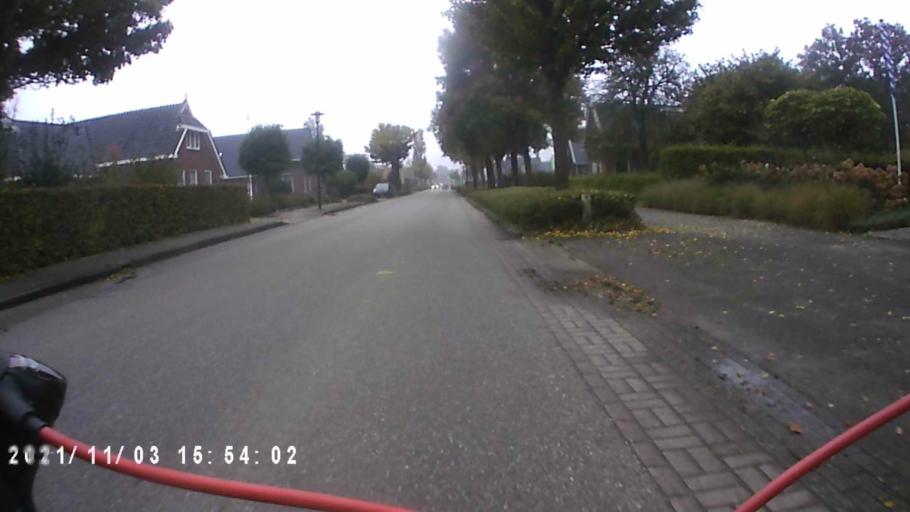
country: NL
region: Groningen
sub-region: Gemeente Leek
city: Leek
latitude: 53.0695
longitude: 6.3321
